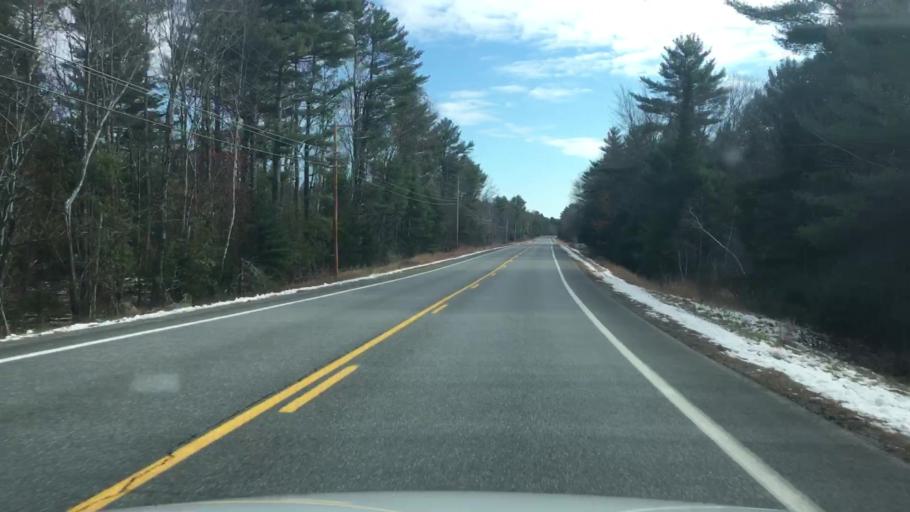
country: US
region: Maine
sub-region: Kennebec County
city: Wayne
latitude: 44.3491
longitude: -70.0488
